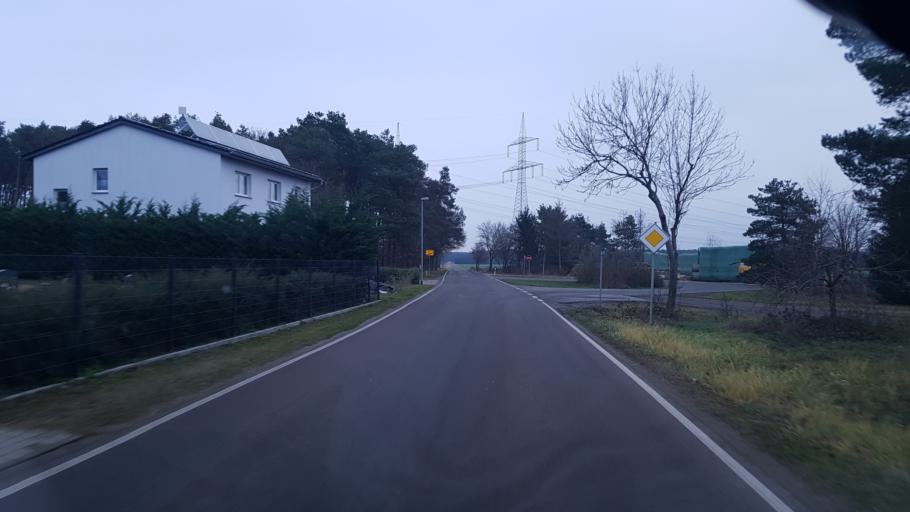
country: DE
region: Brandenburg
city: Briesen
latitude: 51.8570
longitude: 14.2536
